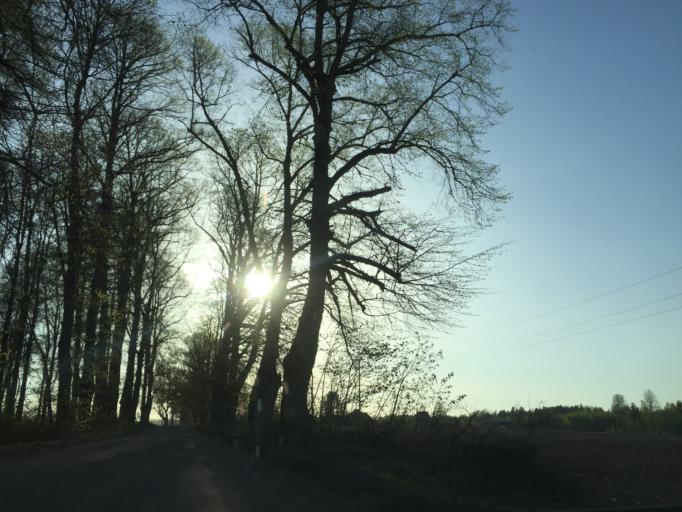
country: LV
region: Ergli
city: Ergli
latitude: 56.7383
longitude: 25.5968
